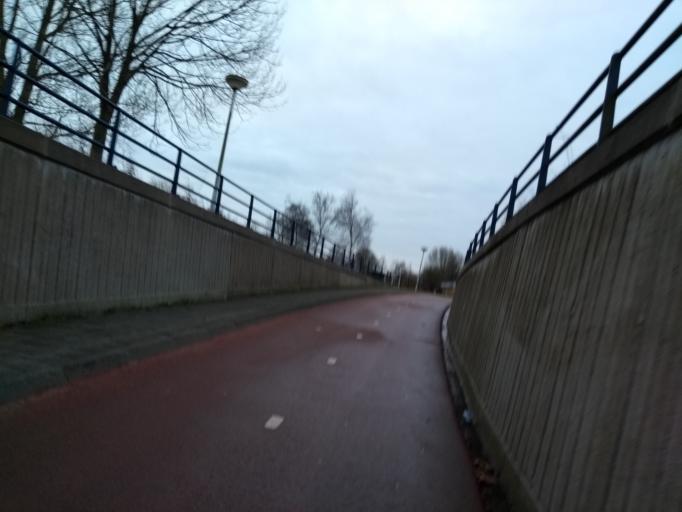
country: NL
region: Friesland
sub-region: Sudwest Fryslan
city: Sneek
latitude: 53.0224
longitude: 5.6482
